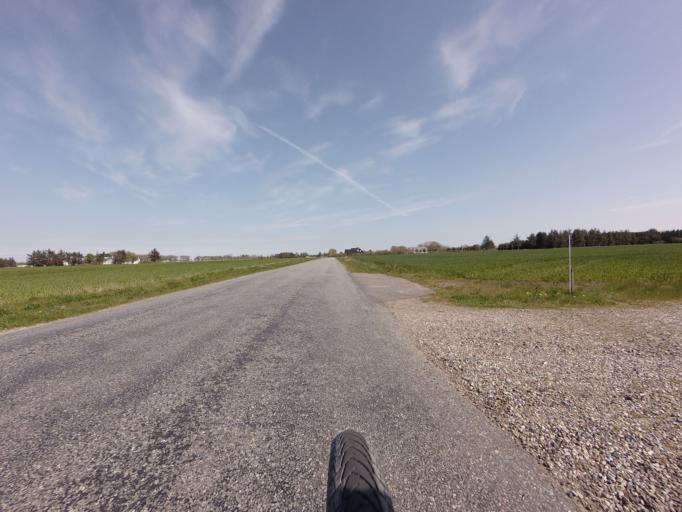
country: DK
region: North Denmark
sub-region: Jammerbugt Kommune
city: Pandrup
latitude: 57.2255
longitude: 9.6525
